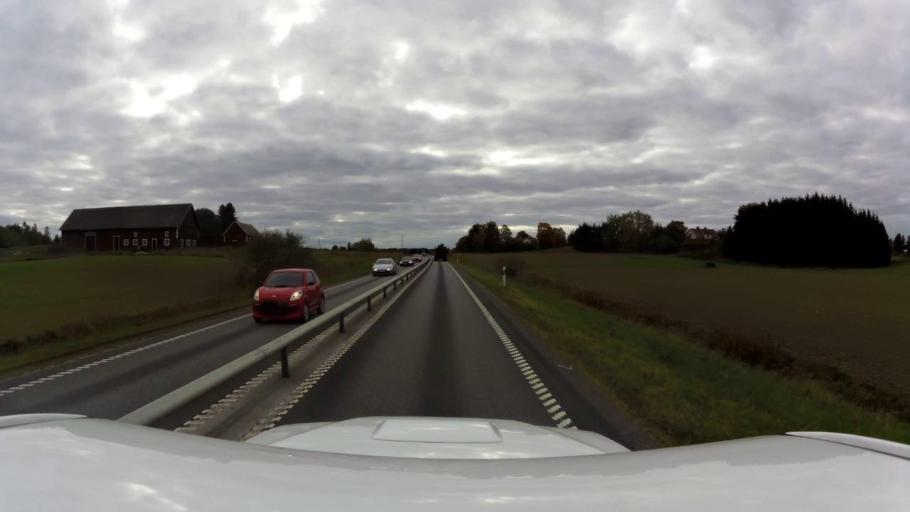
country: SE
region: OEstergoetland
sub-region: Linkopings Kommun
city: Malmslatt
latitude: 58.3369
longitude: 15.5569
